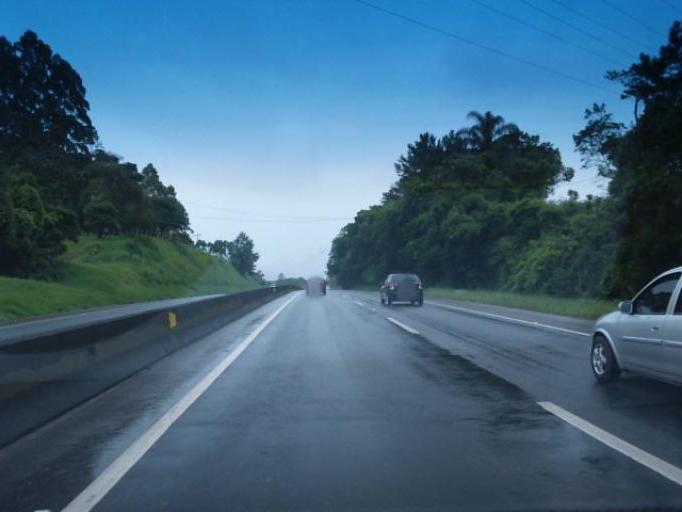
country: BR
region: Santa Catarina
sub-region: Joinville
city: Joinville
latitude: -26.4549
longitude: -48.7687
